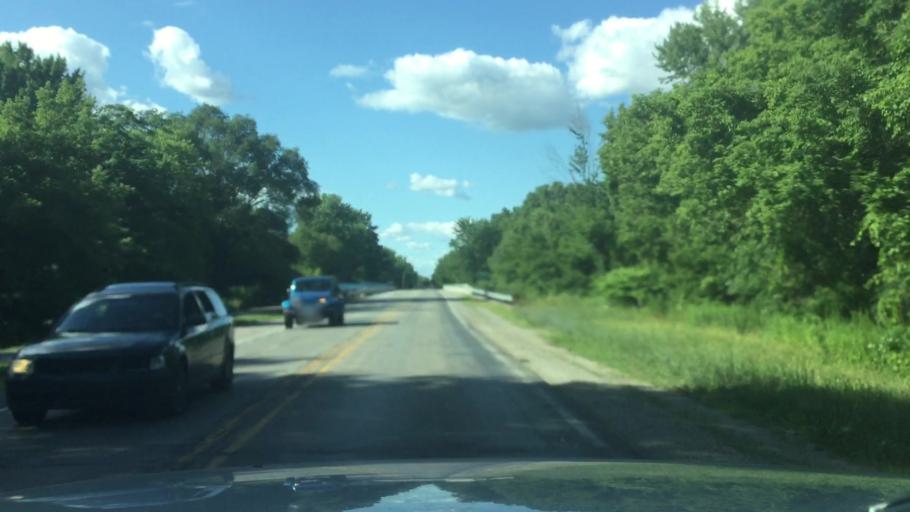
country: US
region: Michigan
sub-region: Saginaw County
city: Shields
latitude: 43.3920
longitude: -84.0149
